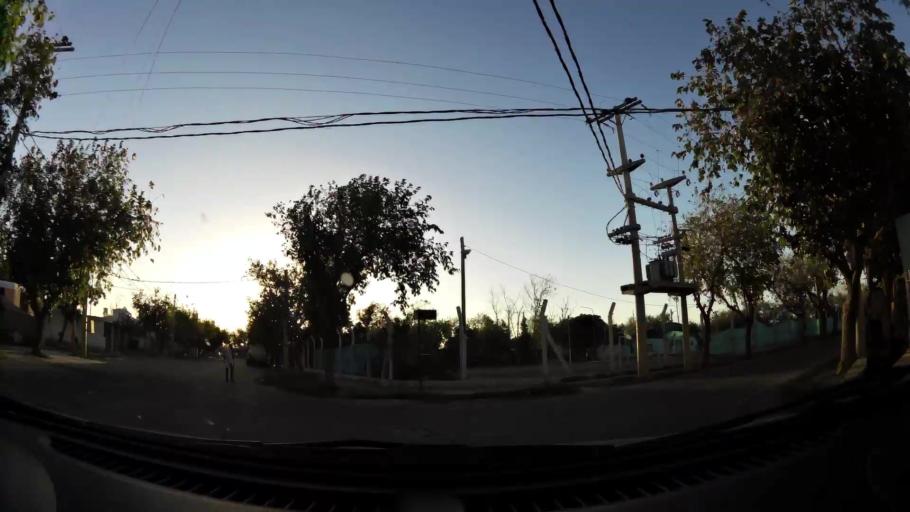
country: AR
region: San Juan
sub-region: Departamento de Santa Lucia
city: Santa Lucia
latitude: -31.5295
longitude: -68.5062
